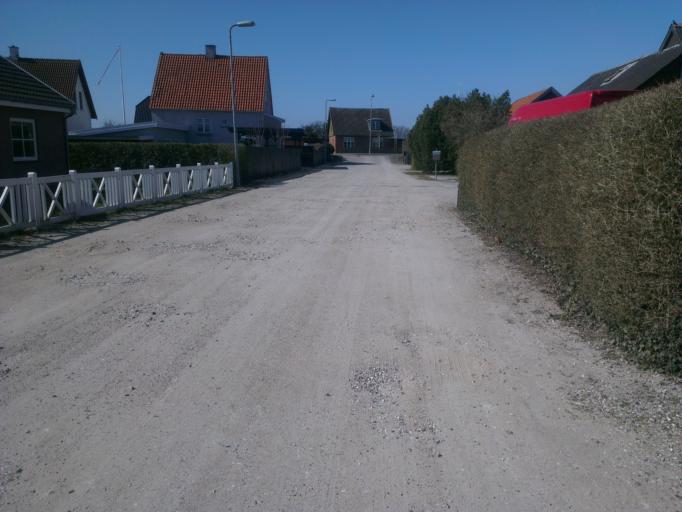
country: DK
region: Capital Region
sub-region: Frederikssund Kommune
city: Frederikssund
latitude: 55.8540
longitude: 12.0644
